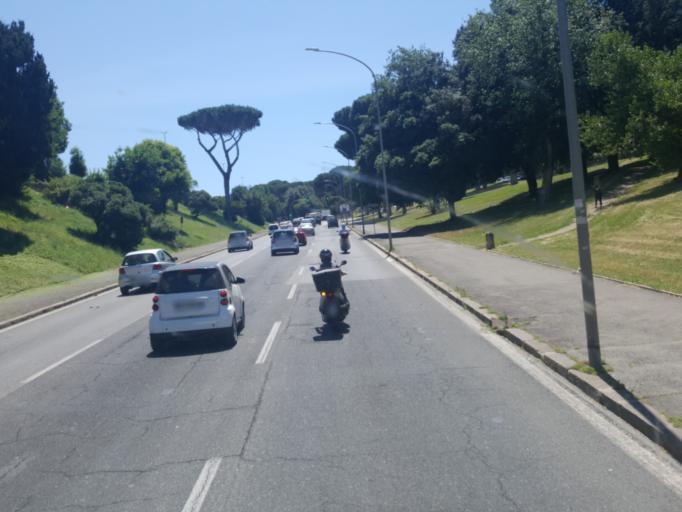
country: IT
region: Latium
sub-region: Citta metropolitana di Roma Capitale
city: Selcetta
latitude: 41.8264
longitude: 12.4653
